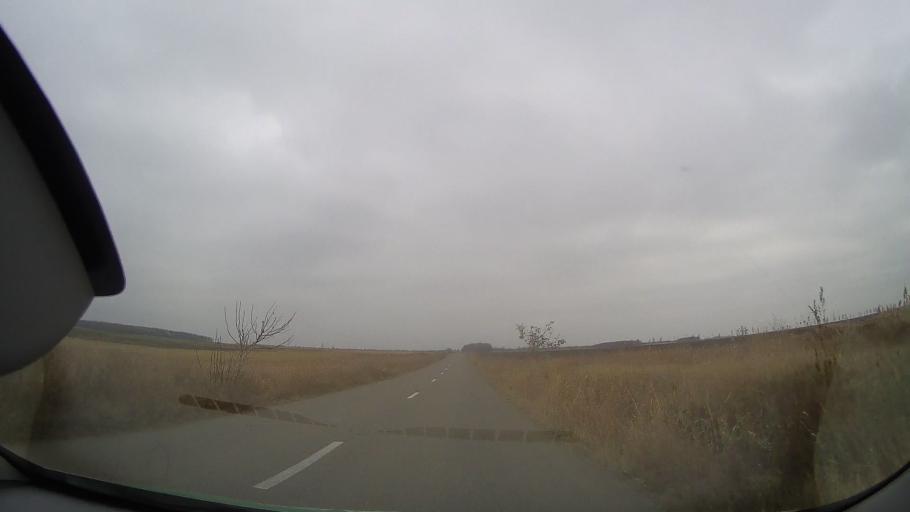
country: RO
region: Buzau
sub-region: Comuna Scutelnici
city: Scutelnici
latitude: 44.8679
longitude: 26.8917
